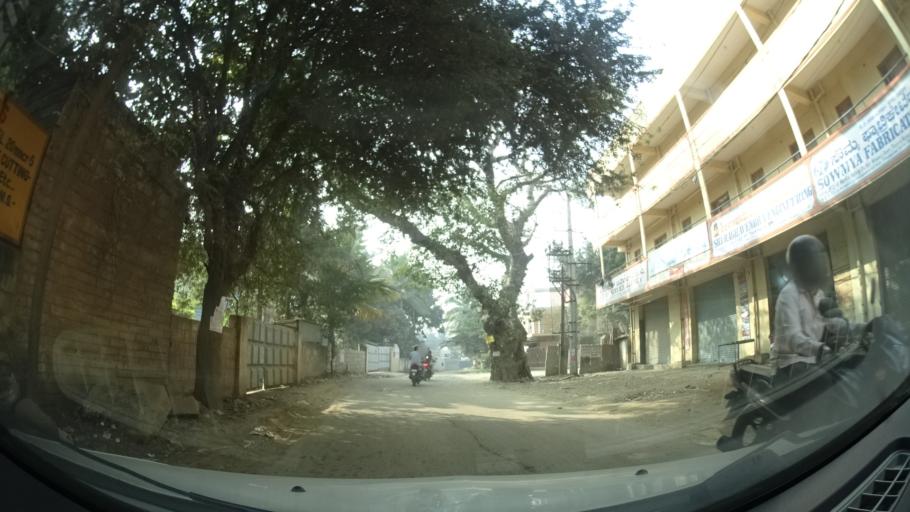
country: IN
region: Karnataka
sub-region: Bangalore Urban
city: Anekal
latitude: 12.8172
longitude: 77.6707
